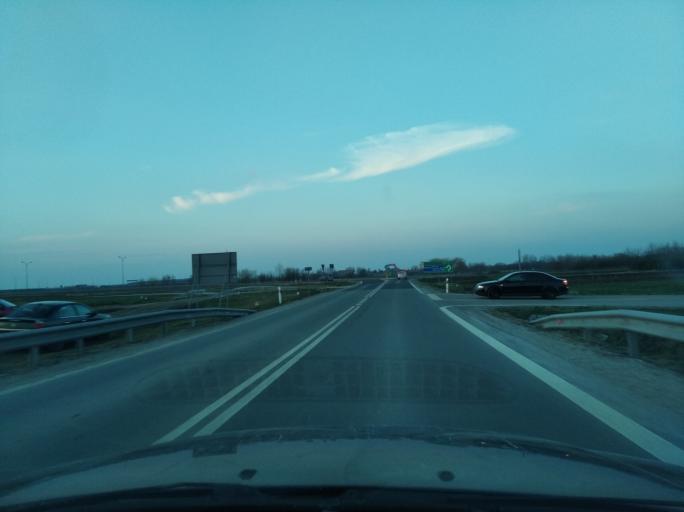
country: PL
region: Subcarpathian Voivodeship
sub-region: Powiat przeworski
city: Gorliczyna
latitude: 50.0786
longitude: 22.4746
